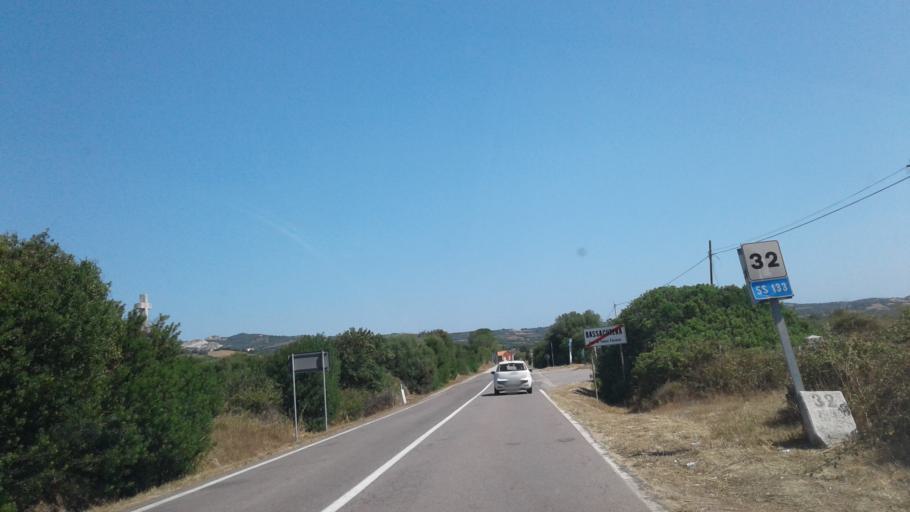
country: IT
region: Sardinia
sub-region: Provincia di Olbia-Tempio
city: Luogosanto
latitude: 41.1115
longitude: 9.2624
